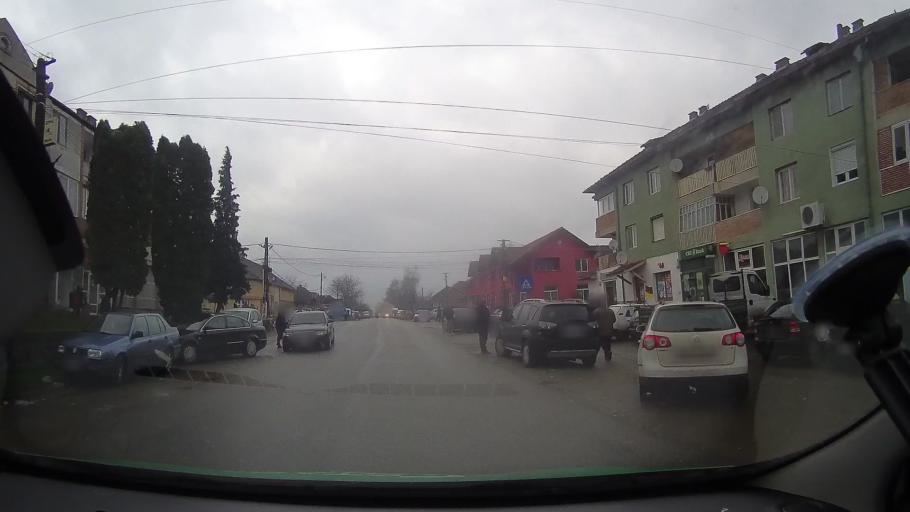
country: RO
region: Arad
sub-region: Comuna Gurahont
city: Gurahont
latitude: 46.2709
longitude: 22.3422
